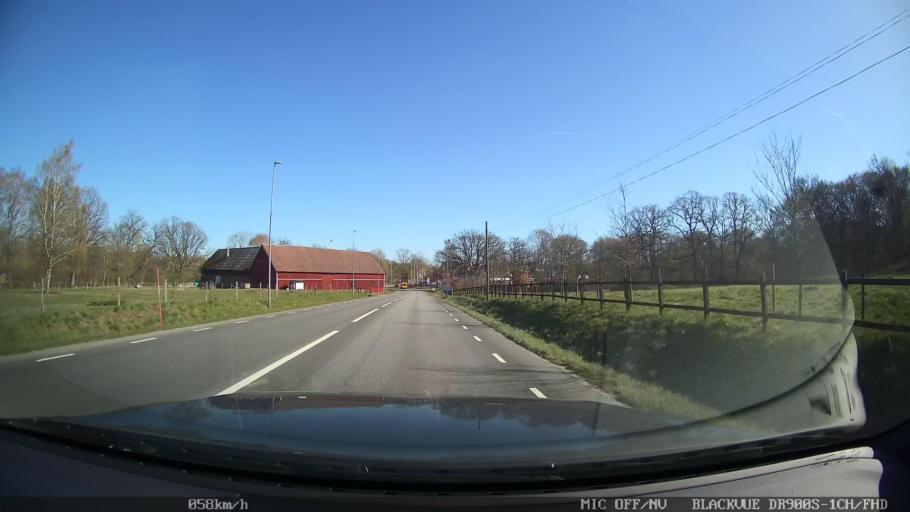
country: SE
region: Skane
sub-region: Klippans Kommun
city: Ljungbyhed
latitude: 56.0042
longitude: 13.2885
